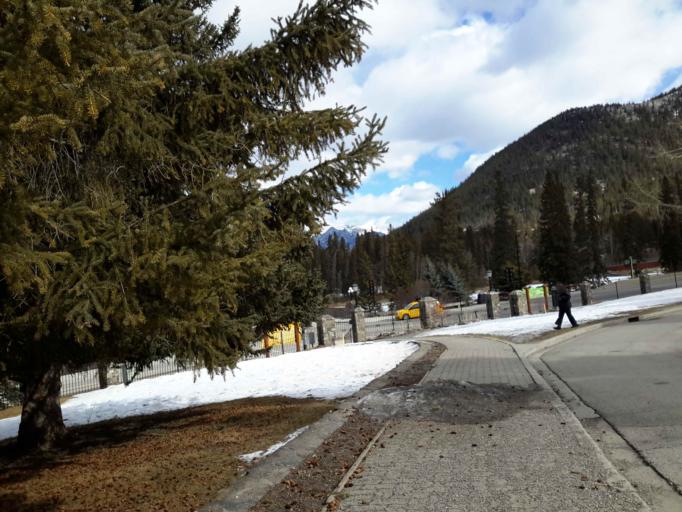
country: CA
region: Alberta
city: Banff
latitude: 51.1716
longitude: -115.5717
